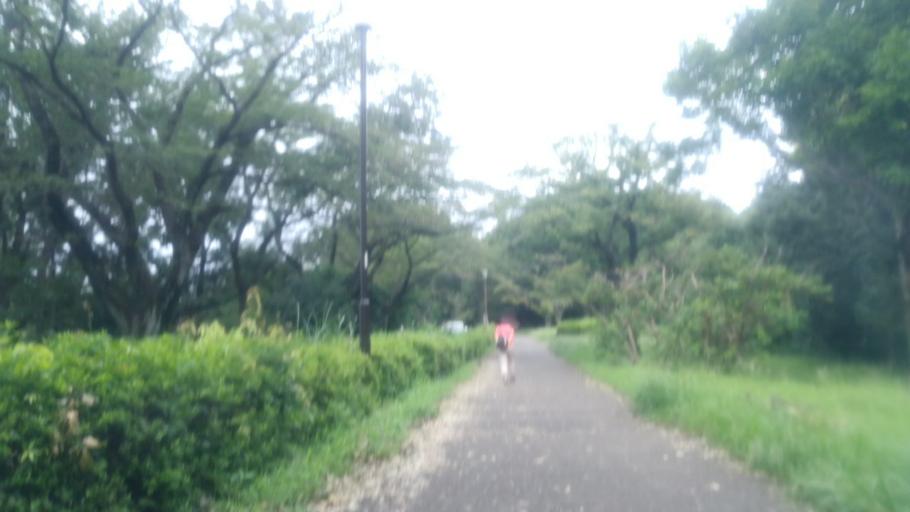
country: JP
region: Tokyo
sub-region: Machida-shi
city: Machida
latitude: 35.5877
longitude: 139.4004
